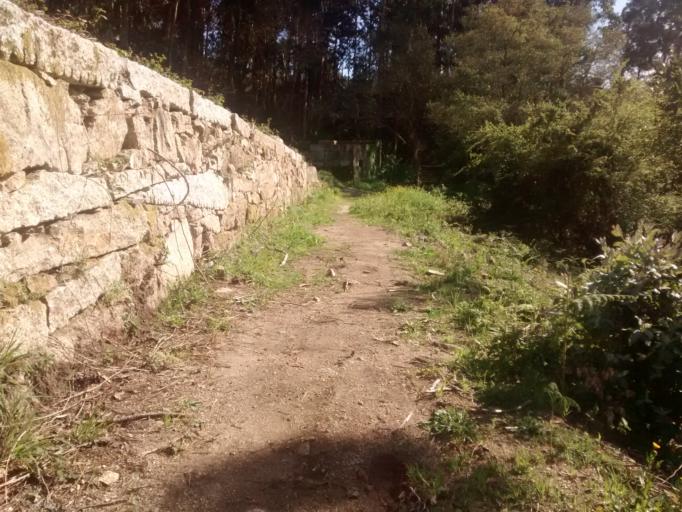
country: ES
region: Galicia
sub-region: Provincia de Pontevedra
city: O Grove
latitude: 42.4831
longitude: -8.8874
